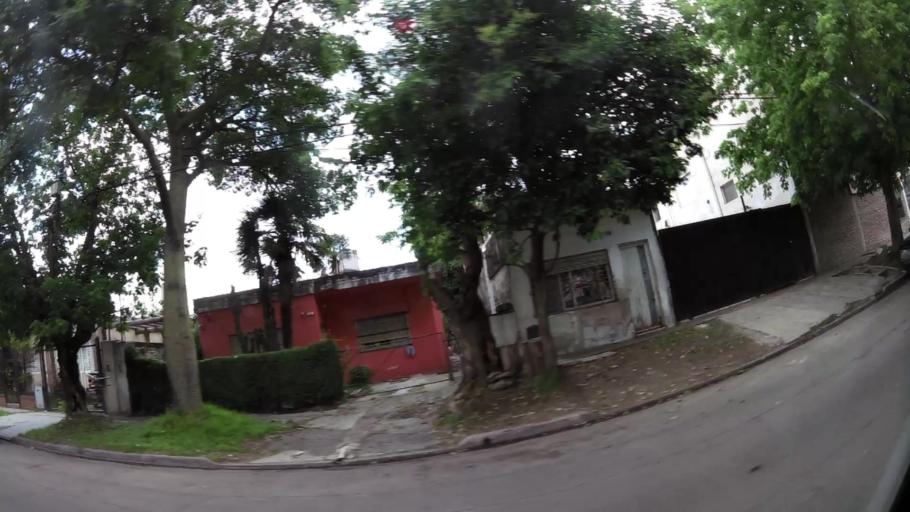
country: AR
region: Buenos Aires
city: Ituzaingo
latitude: -34.6404
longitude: -58.6770
